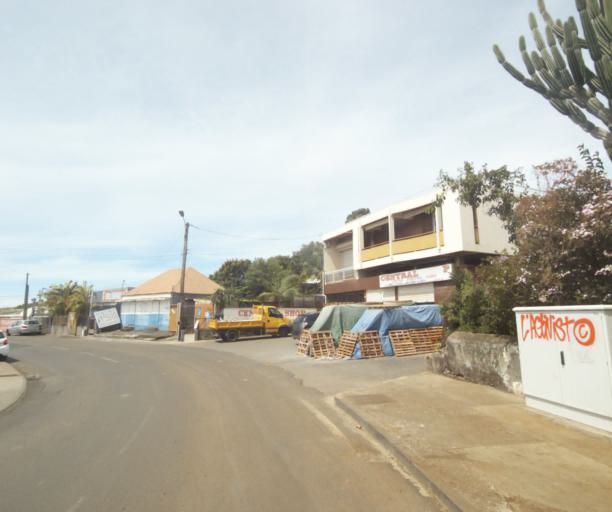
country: RE
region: Reunion
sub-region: Reunion
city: Saint-Paul
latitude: -21.0465
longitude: 55.2858
